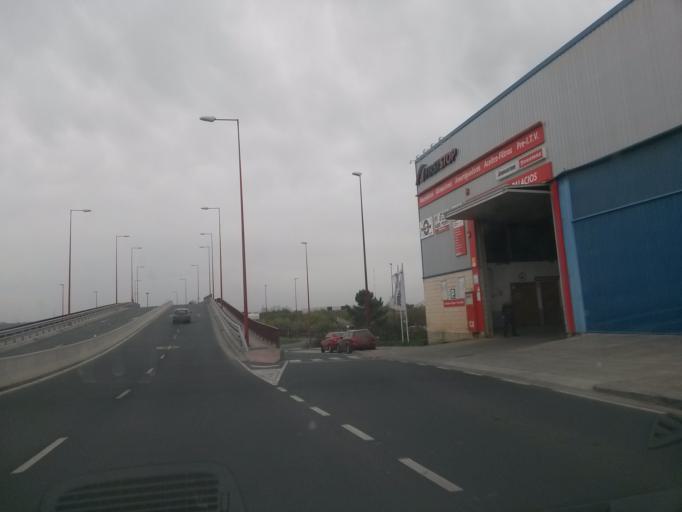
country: ES
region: Galicia
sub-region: Provincia de Lugo
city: Lugo
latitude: 43.0434
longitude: -7.5593
